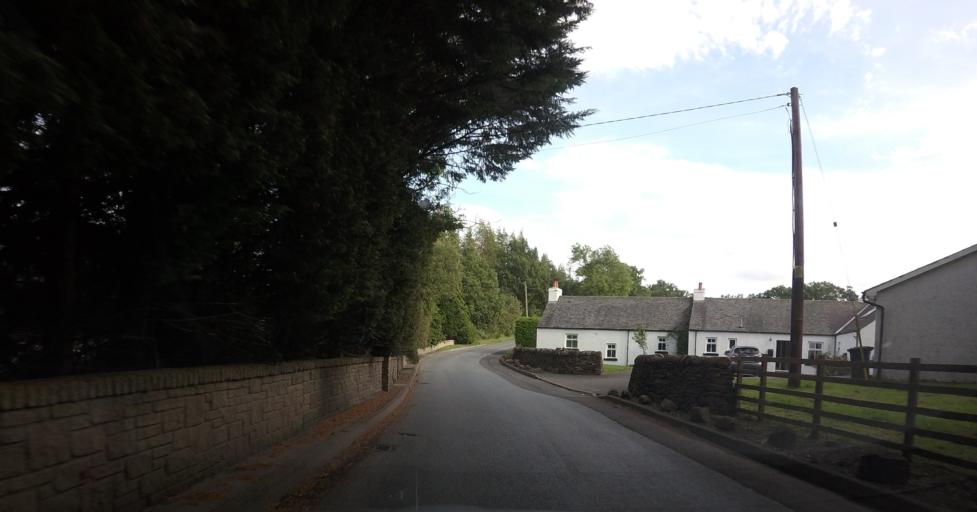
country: GB
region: Scotland
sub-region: Perth and Kinross
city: Auchterarder
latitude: 56.3066
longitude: -3.7290
